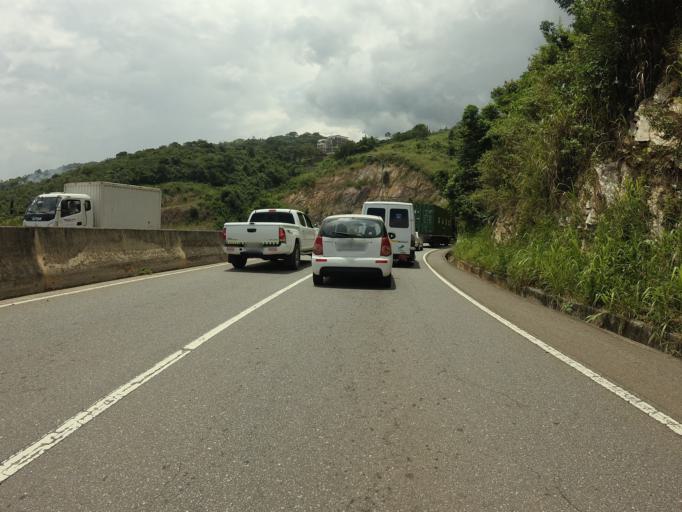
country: GH
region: Eastern
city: Aburi
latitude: 5.7947
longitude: -0.1855
